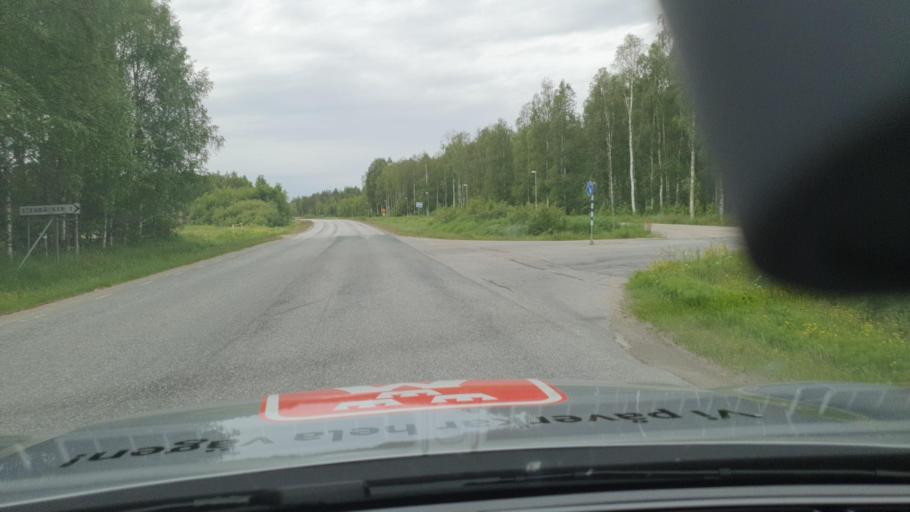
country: SE
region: Norrbotten
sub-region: Kalix Kommun
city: Rolfs
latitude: 65.8706
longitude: 23.1141
